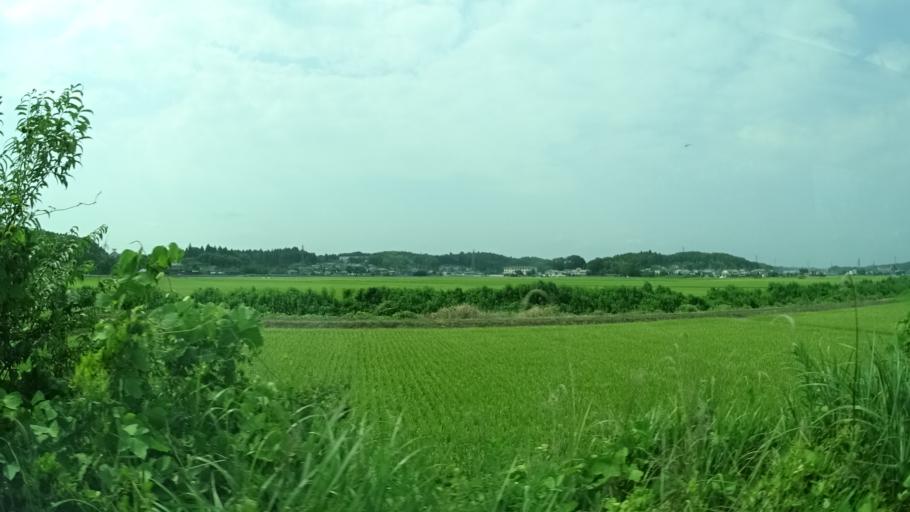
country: JP
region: Tochigi
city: Mashiko
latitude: 36.5268
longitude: 140.0987
